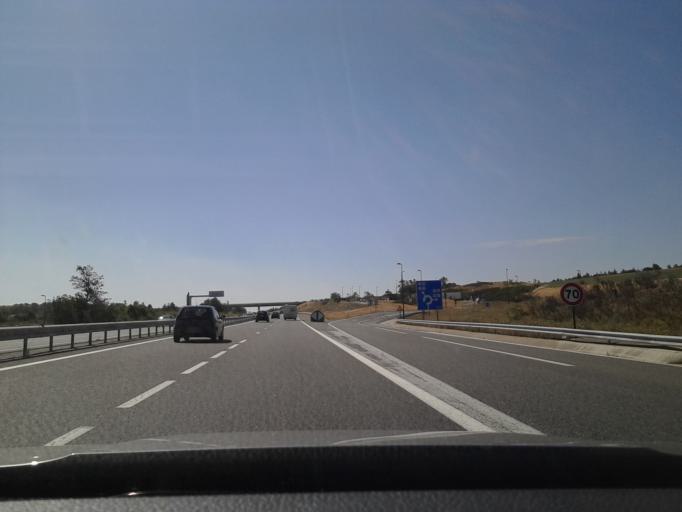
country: FR
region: Midi-Pyrenees
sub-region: Departement de l'Aveyron
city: La Cavalerie
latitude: 43.9828
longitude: 3.1845
